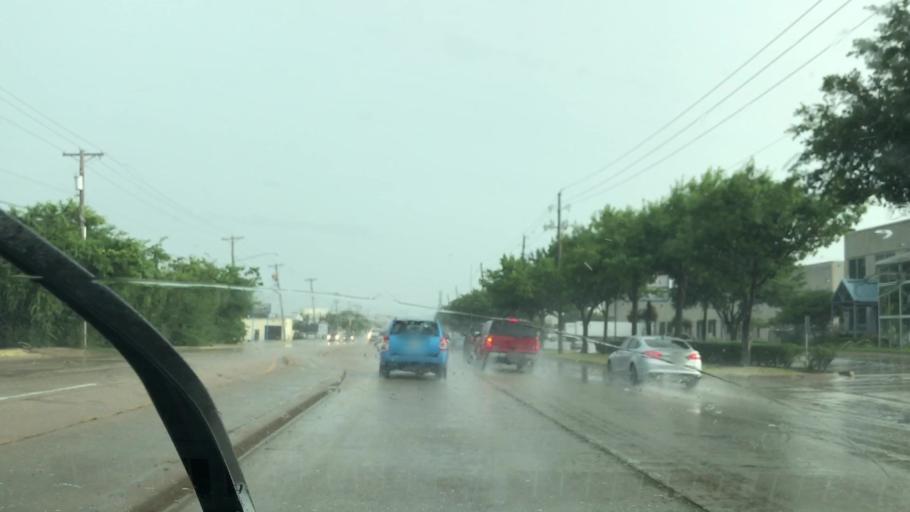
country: US
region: Texas
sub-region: Dallas County
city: Richardson
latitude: 32.8928
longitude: -96.7004
